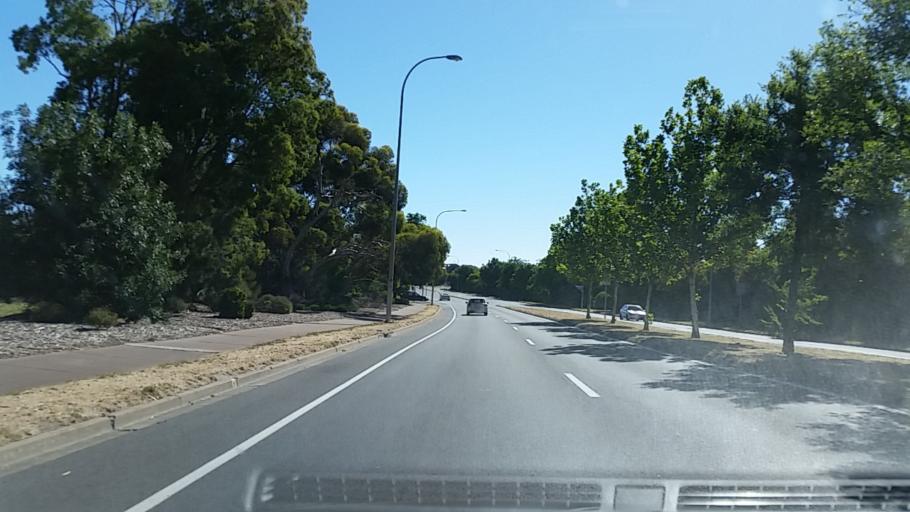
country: AU
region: South Australia
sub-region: Tea Tree Gully
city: Modbury
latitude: -34.7940
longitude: 138.6913
